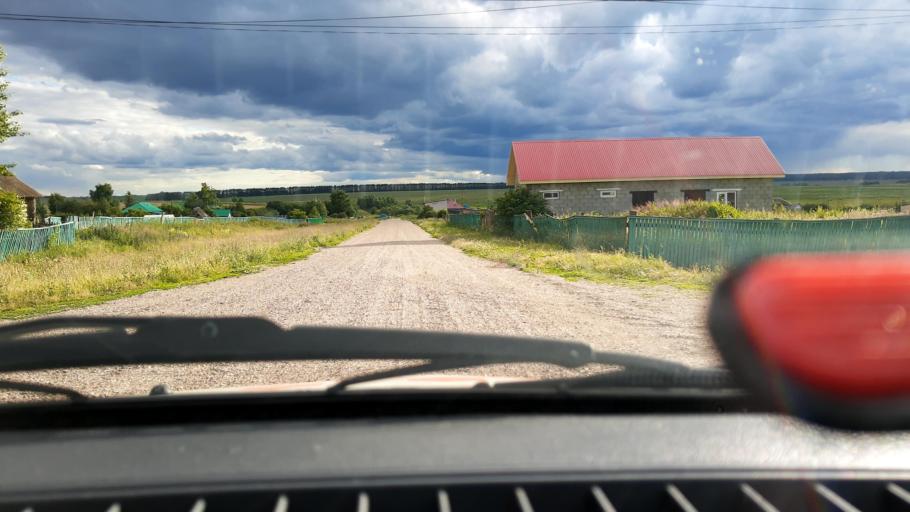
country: RU
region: Bashkortostan
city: Karmaskaly
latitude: 54.4228
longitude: 56.0253
